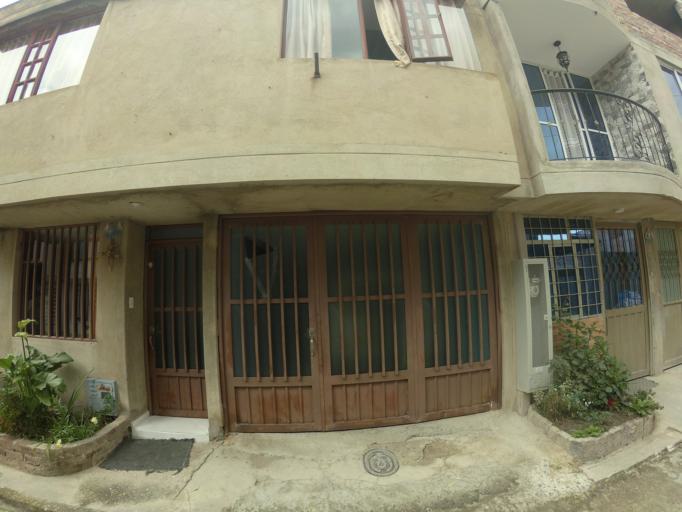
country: CO
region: Boyaca
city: Duitama
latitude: 5.8325
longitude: -73.0422
